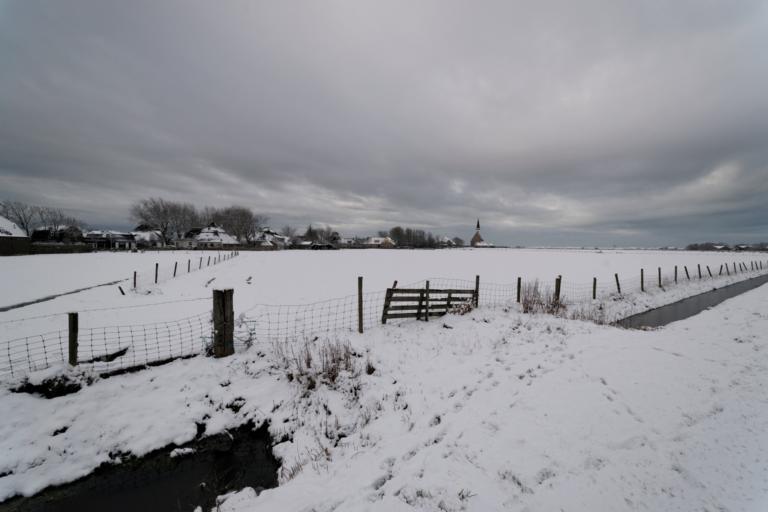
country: NL
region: North Holland
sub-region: Gemeente Texel
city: Den Burg
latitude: 53.0266
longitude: 4.7579
